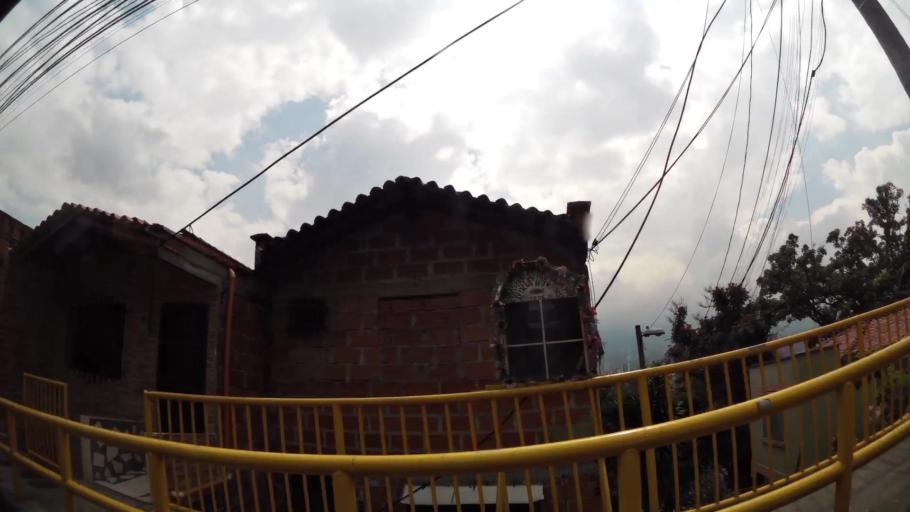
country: CO
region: Antioquia
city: Itagui
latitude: 6.2001
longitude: -75.5905
